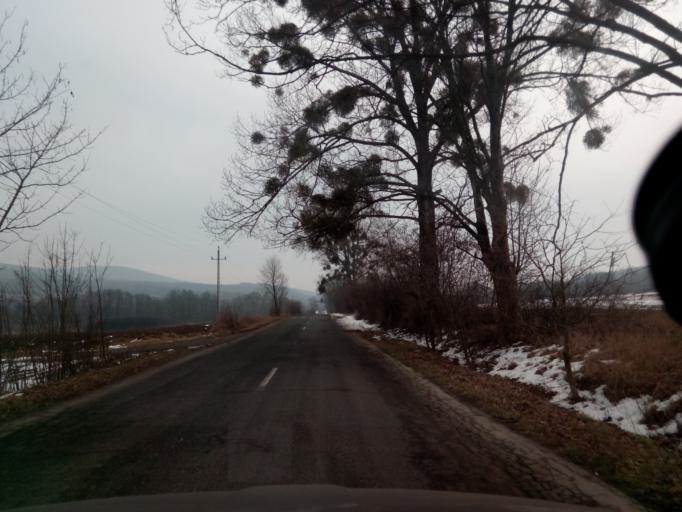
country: HU
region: Borsod-Abauj-Zemplen
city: Gonc
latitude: 48.5069
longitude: 21.3189
